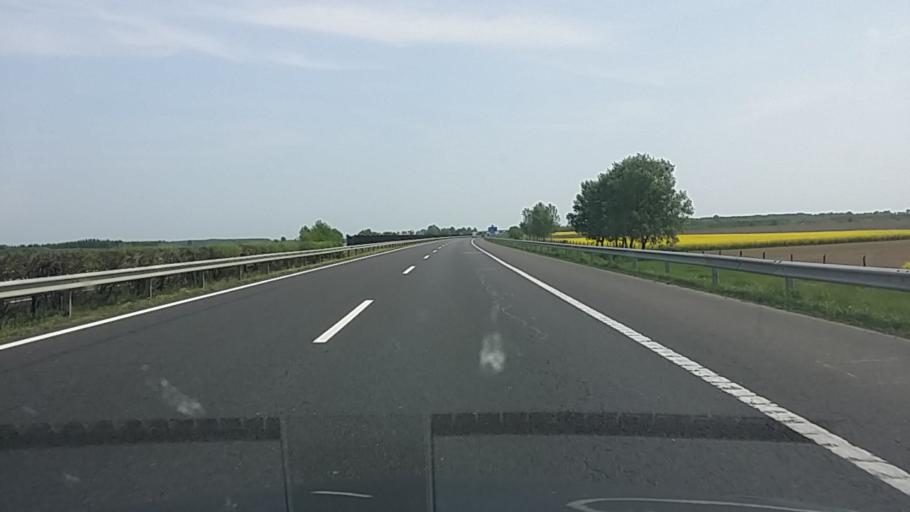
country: HU
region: Borsod-Abauj-Zemplen
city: Hejobaba
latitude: 47.8836
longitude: 20.8803
